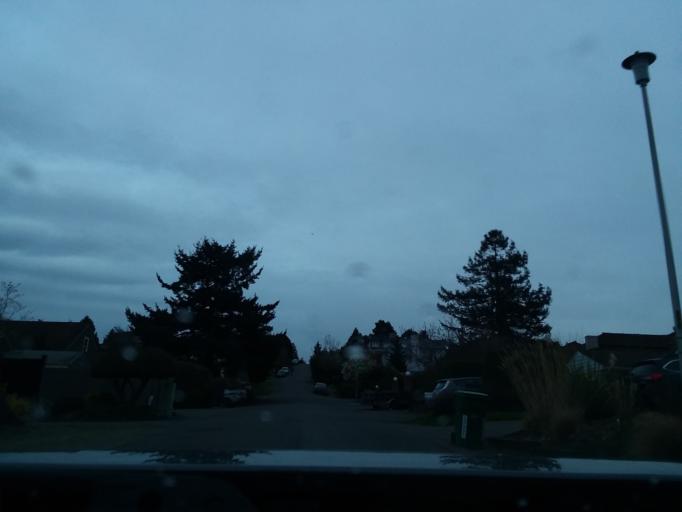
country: US
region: Washington
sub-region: King County
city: Shoreline
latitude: 47.6982
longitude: -122.3862
